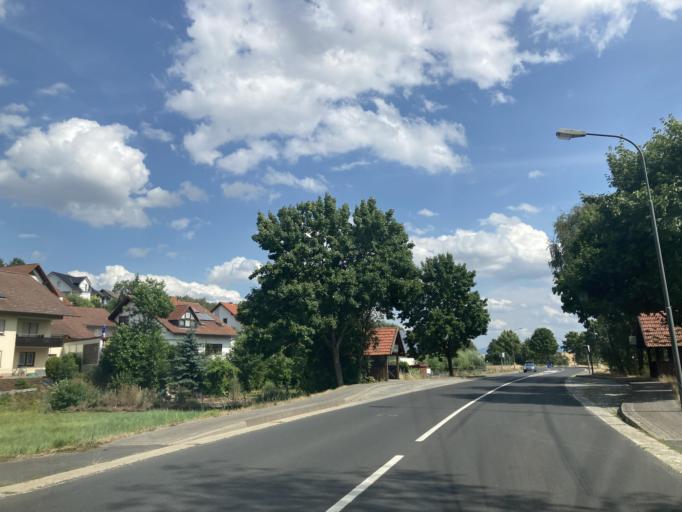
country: DE
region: Hesse
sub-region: Regierungsbezirk Kassel
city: Fulda
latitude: 50.5408
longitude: 9.6069
